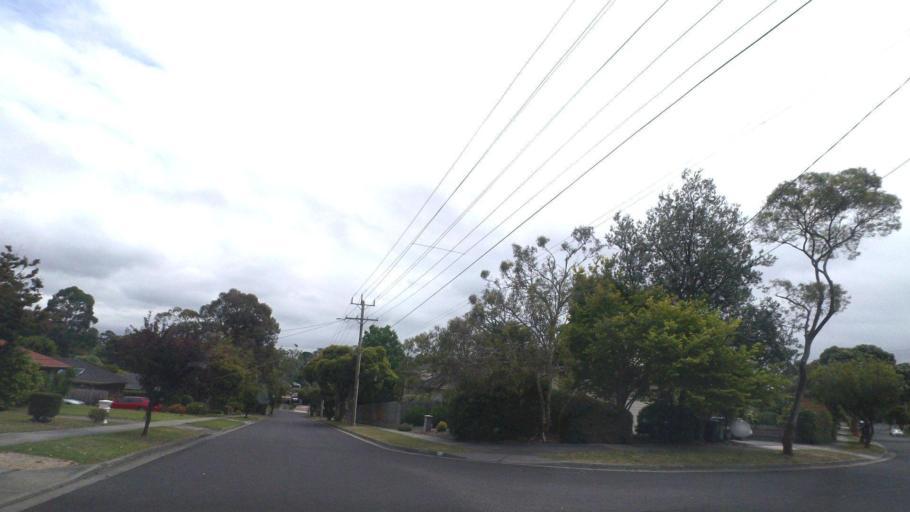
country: AU
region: Victoria
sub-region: Knox
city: The Basin
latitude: -37.8532
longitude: 145.3070
